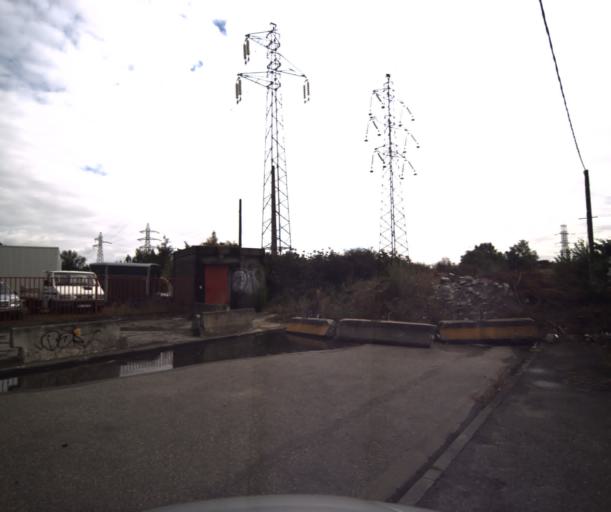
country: FR
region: Midi-Pyrenees
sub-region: Departement de la Haute-Garonne
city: Pinsaguel
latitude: 43.5266
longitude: 1.3804
